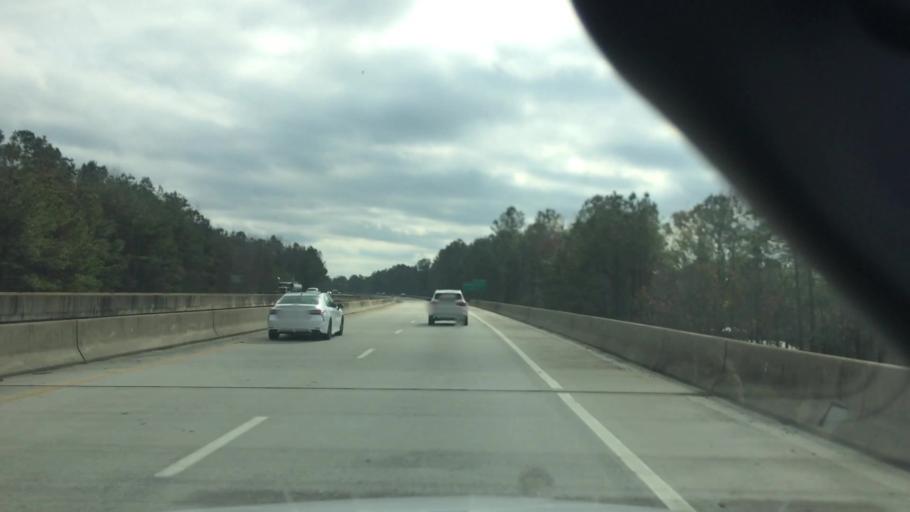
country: US
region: North Carolina
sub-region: New Hanover County
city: Castle Hayne
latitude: 34.3641
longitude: -77.8885
